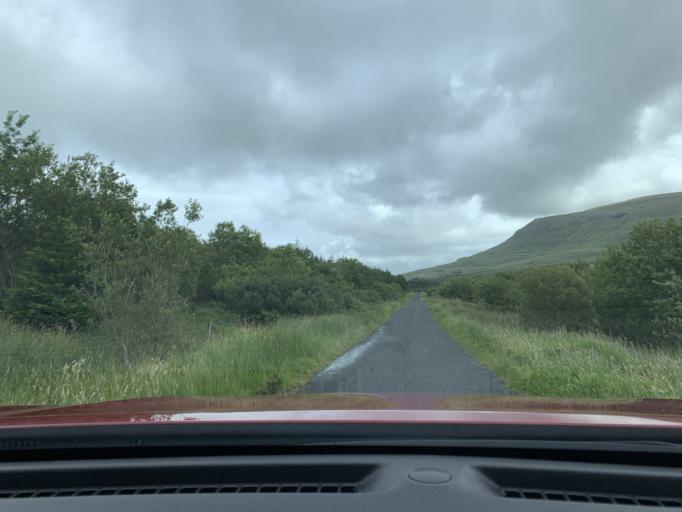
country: IE
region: Connaught
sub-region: Sligo
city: Sligo
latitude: 54.3832
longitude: -8.4110
